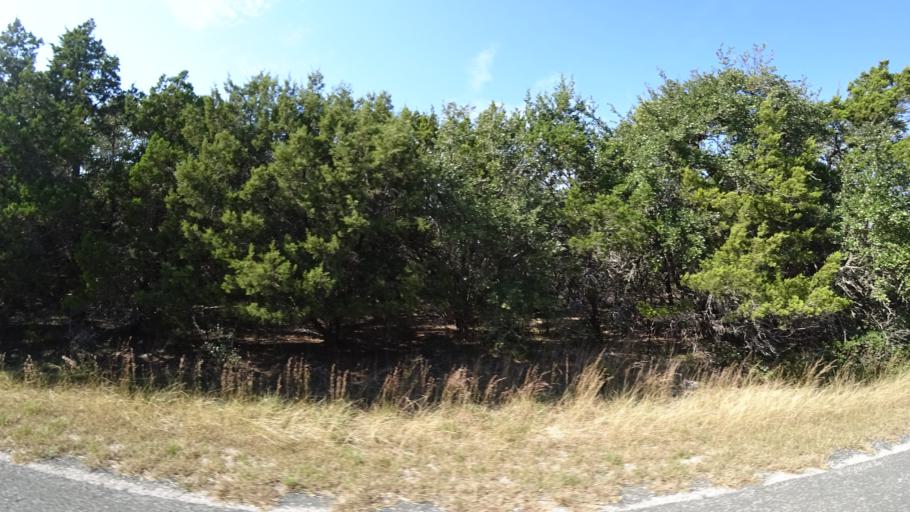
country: US
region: Texas
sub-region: Travis County
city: Bee Cave
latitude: 30.2211
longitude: -97.9363
